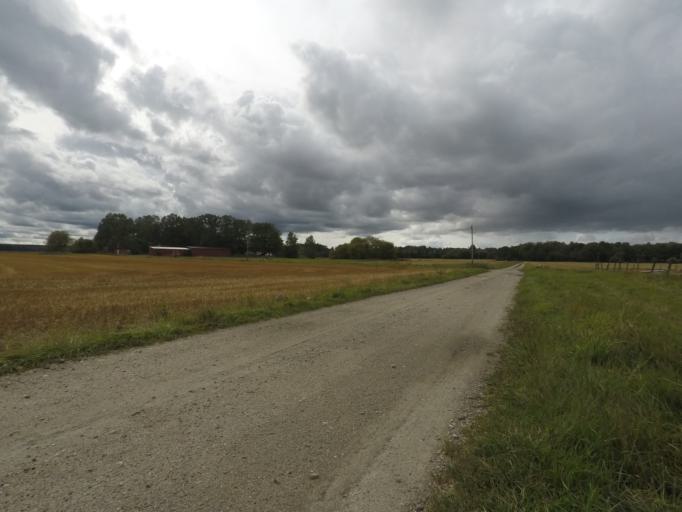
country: SE
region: Vaestmanland
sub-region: Kungsors Kommun
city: Kungsoer
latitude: 59.4550
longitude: 16.0597
